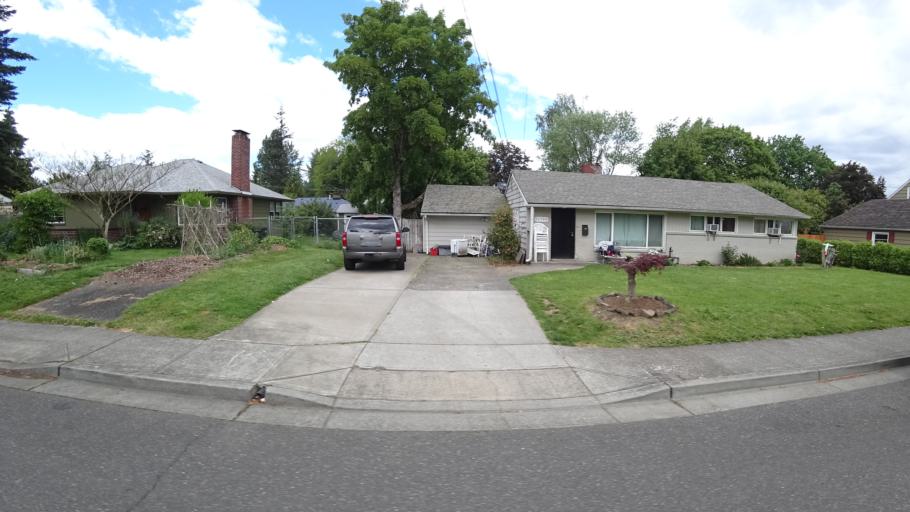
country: US
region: Oregon
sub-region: Washington County
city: Beaverton
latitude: 45.4786
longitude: -122.7981
